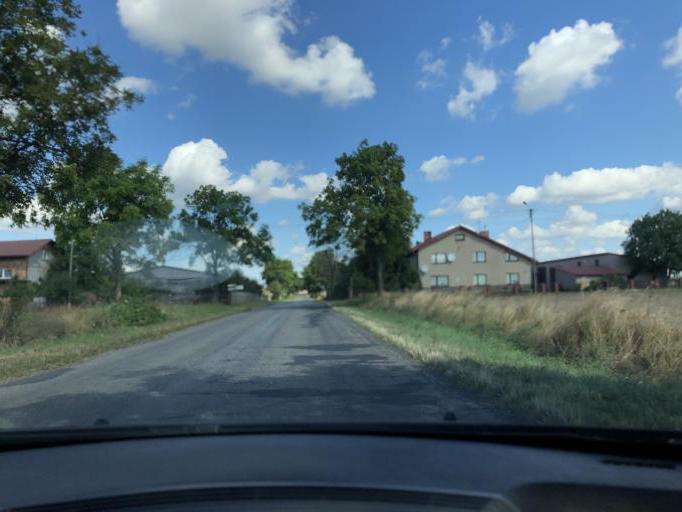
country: PL
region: Lodz Voivodeship
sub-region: Powiat wieruszowski
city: Czastary
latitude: 51.2507
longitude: 18.3172
